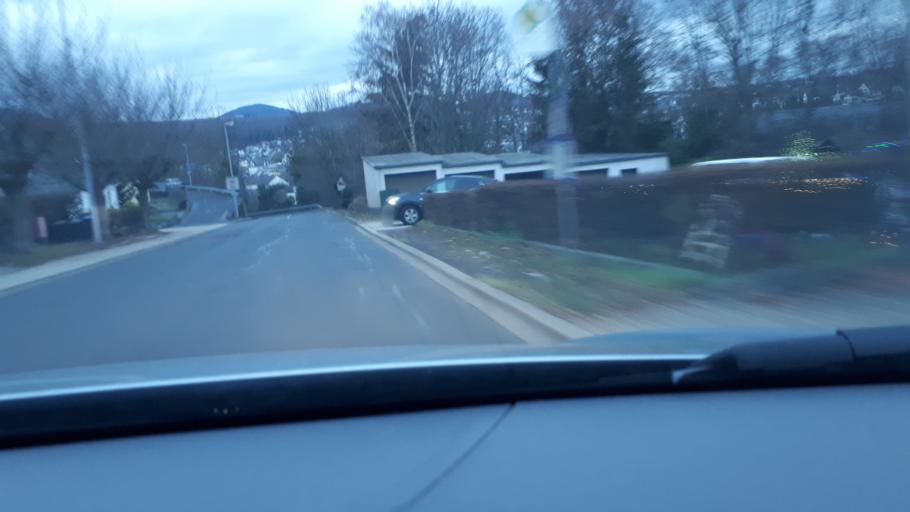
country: DE
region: Rheinland-Pfalz
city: Mayen
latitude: 50.3218
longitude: 7.2261
